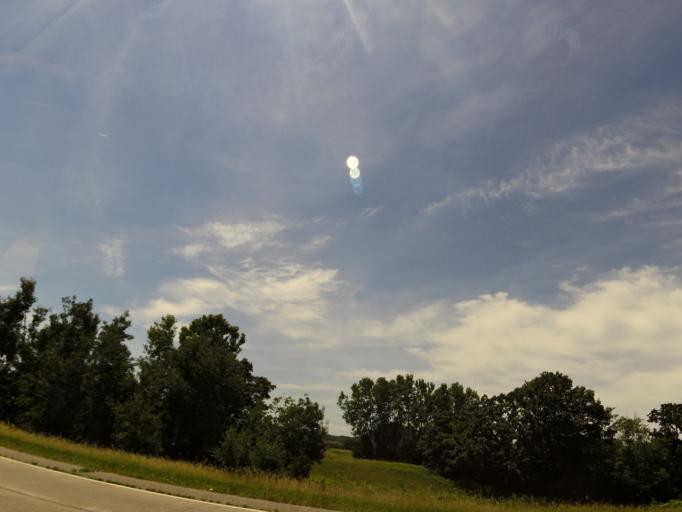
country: US
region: Minnesota
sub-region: Scott County
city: Prior Lake
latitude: 44.7830
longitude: -93.4199
